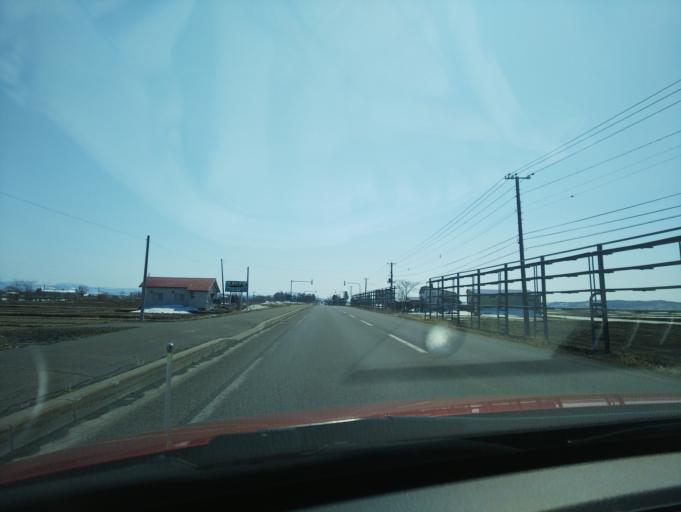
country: JP
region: Hokkaido
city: Nayoro
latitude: 44.2291
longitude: 142.3948
